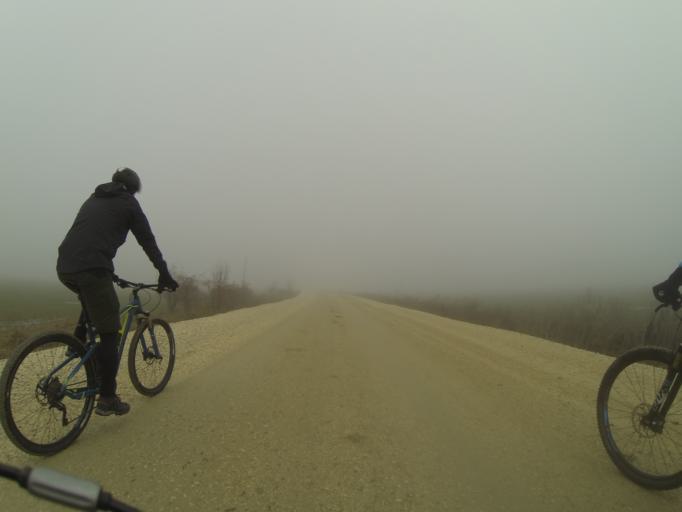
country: RO
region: Mehedinti
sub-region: Comuna Balacita
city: Gvardinita
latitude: 44.4383
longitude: 23.1358
